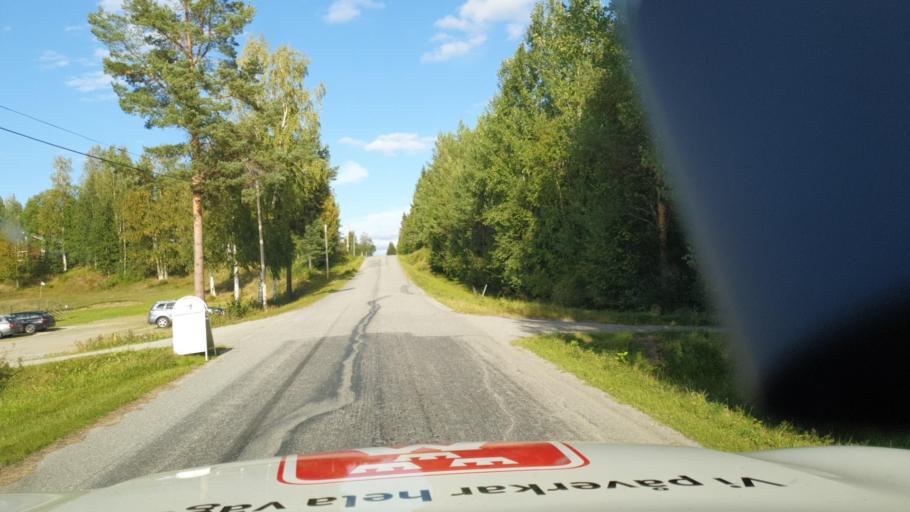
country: SE
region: Vaesterbotten
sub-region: Dorotea Kommun
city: Dorotea
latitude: 63.9145
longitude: 16.3227
